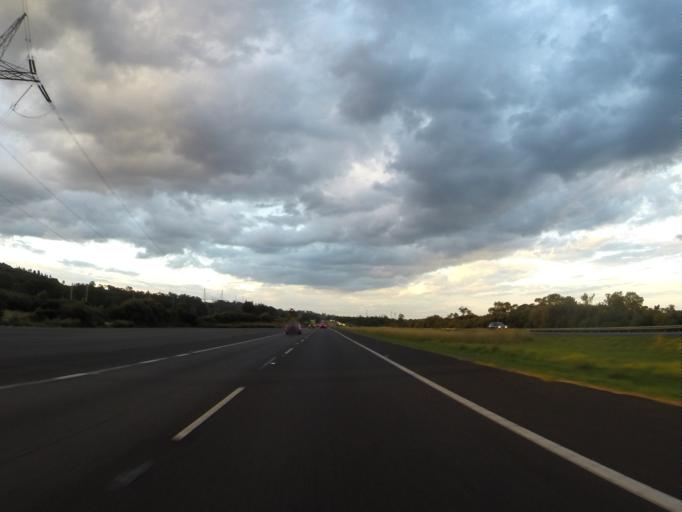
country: AU
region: New South Wales
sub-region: Campbelltown Municipality
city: Glen Alpine
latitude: -34.0846
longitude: 150.7701
